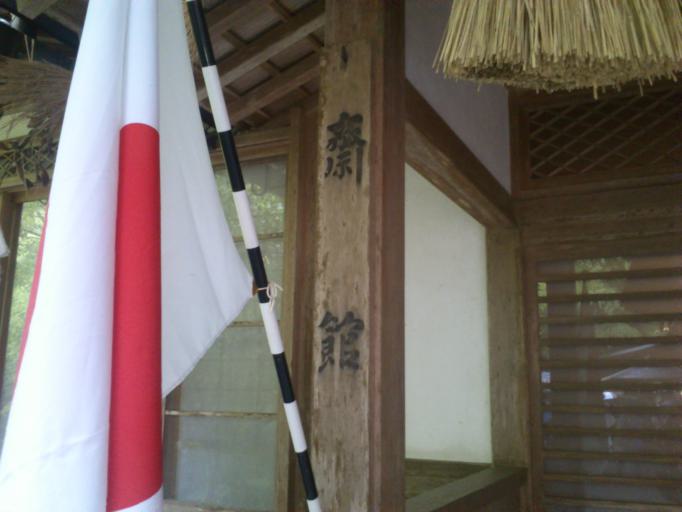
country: JP
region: Kyoto
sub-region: Kyoto-shi
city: Kamigyo-ku
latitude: 35.1240
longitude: 135.7658
